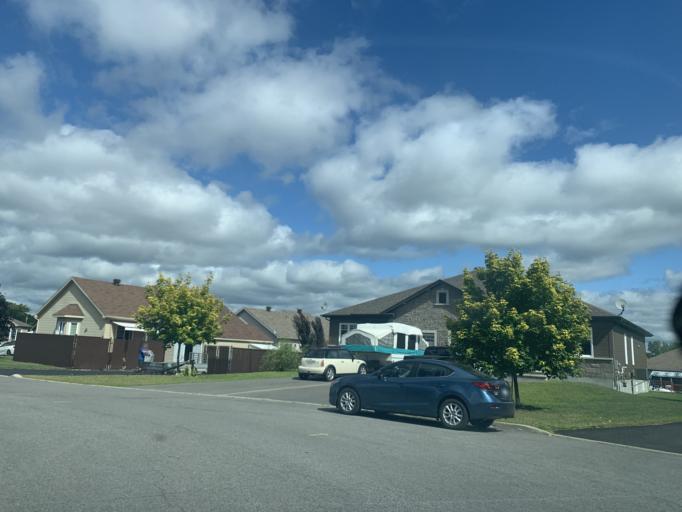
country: CA
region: Ontario
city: Hawkesbury
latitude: 45.6017
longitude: -74.5809
